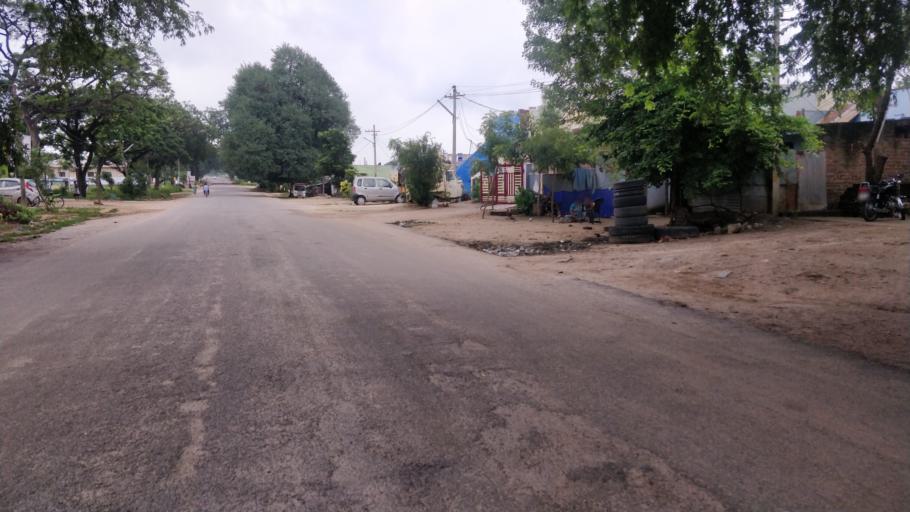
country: IN
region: Telangana
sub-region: Medak
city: Narsingi
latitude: 18.1833
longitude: 78.3974
